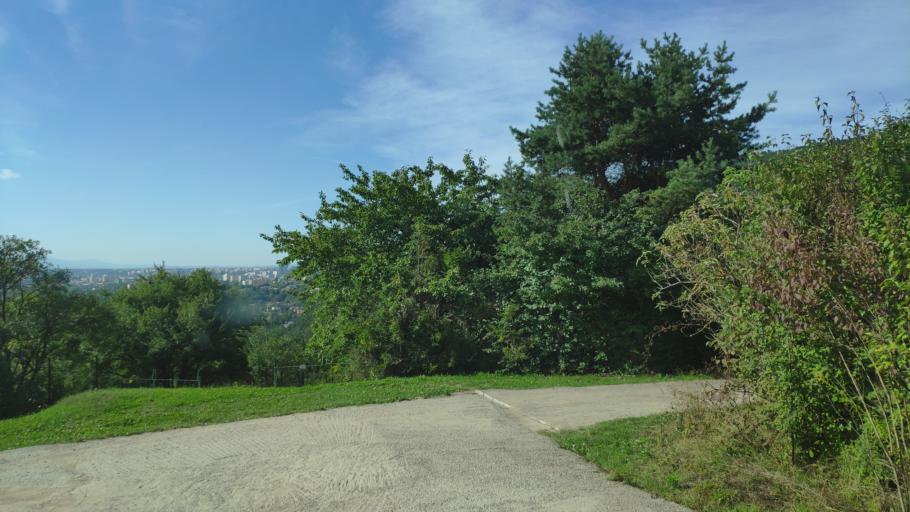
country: SK
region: Kosicky
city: Kosice
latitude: 48.7655
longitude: 21.2503
